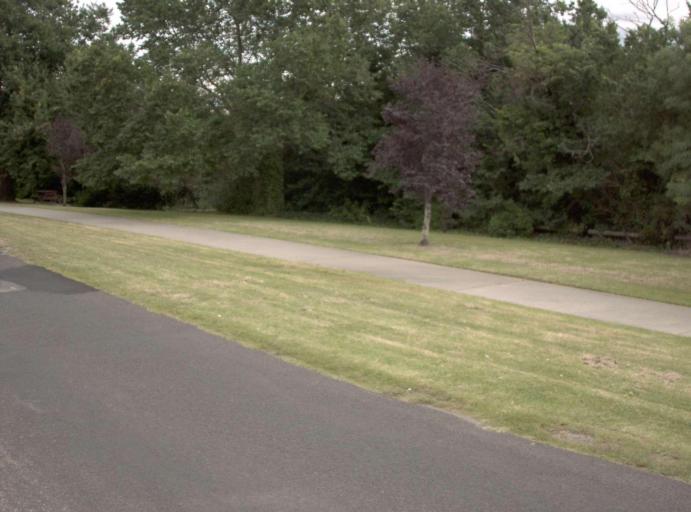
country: AU
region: Victoria
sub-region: East Gippsland
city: Bairnsdale
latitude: -37.8212
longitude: 147.6241
